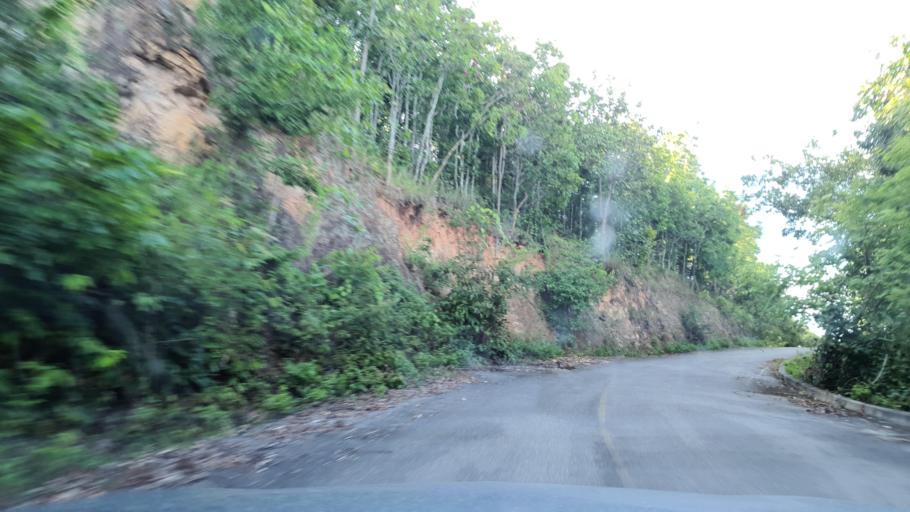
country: TH
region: Chiang Mai
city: Mae On
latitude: 18.7692
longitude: 99.2889
